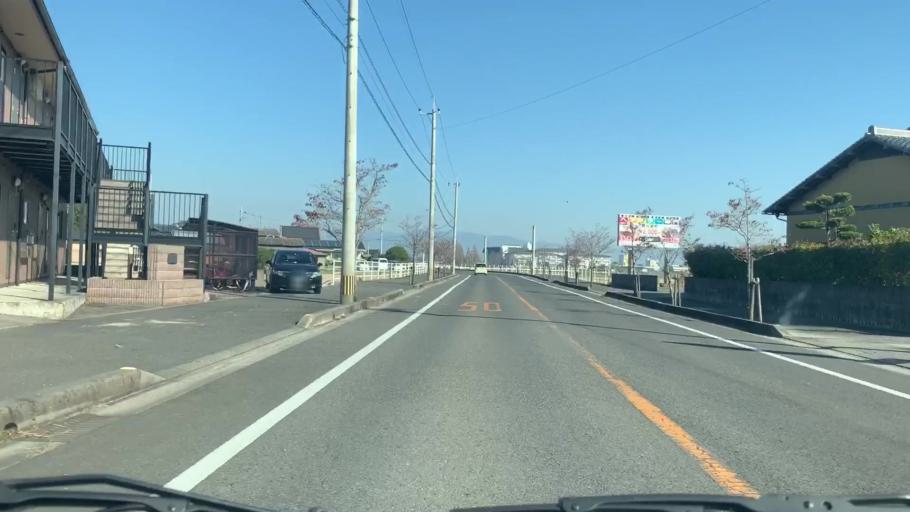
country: JP
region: Saga Prefecture
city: Saga-shi
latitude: 33.2325
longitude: 130.3125
